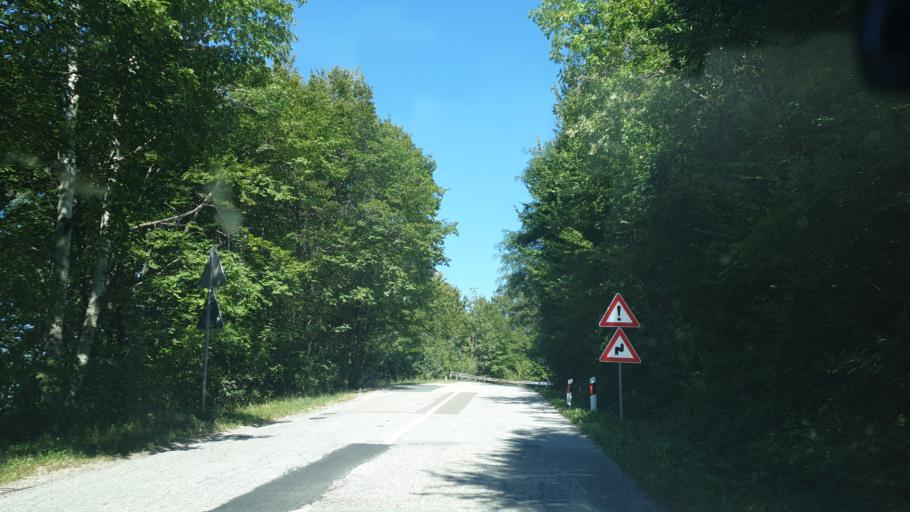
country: RS
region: Central Serbia
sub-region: Kolubarski Okrug
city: Mionica
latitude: 44.1527
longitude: 20.0130
